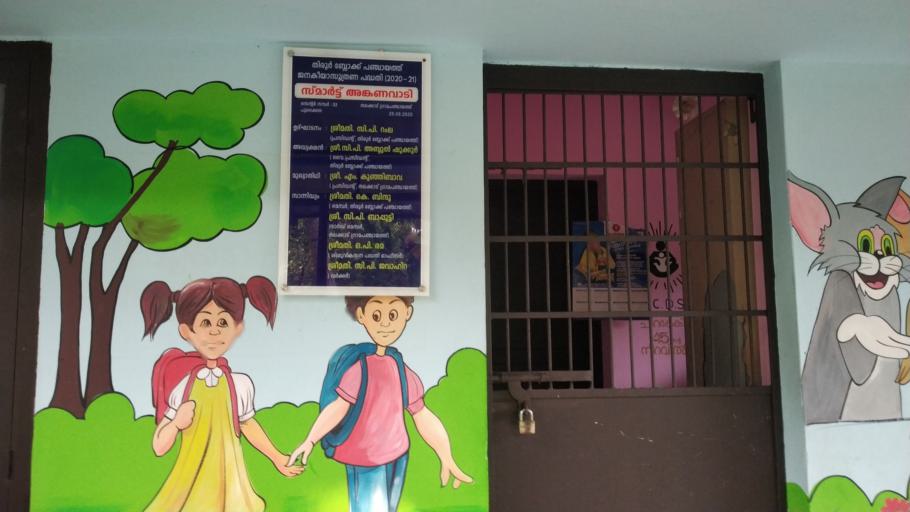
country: IN
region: Kerala
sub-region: Malappuram
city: Tirur
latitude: 10.8809
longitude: 75.9240
